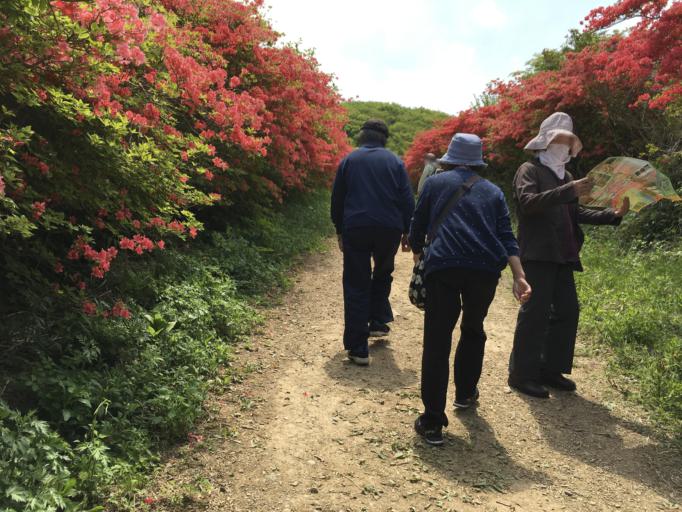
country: JP
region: Iwate
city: Ofunato
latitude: 38.8505
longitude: 141.4714
